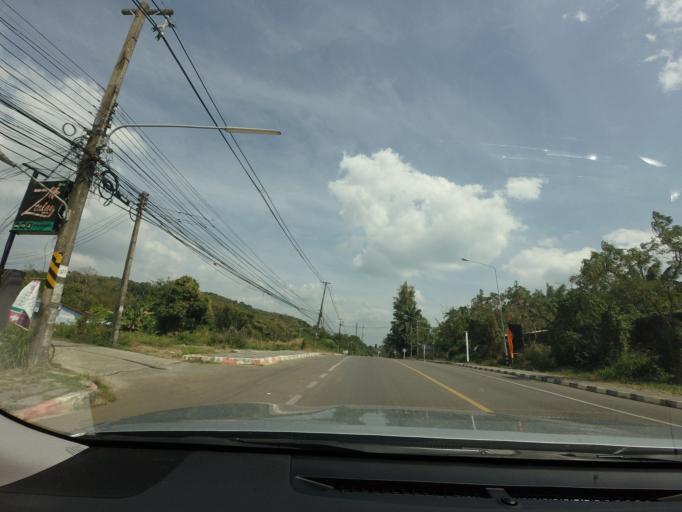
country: TH
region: Phangnga
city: Ban Ao Nang
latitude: 8.0554
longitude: 98.7523
